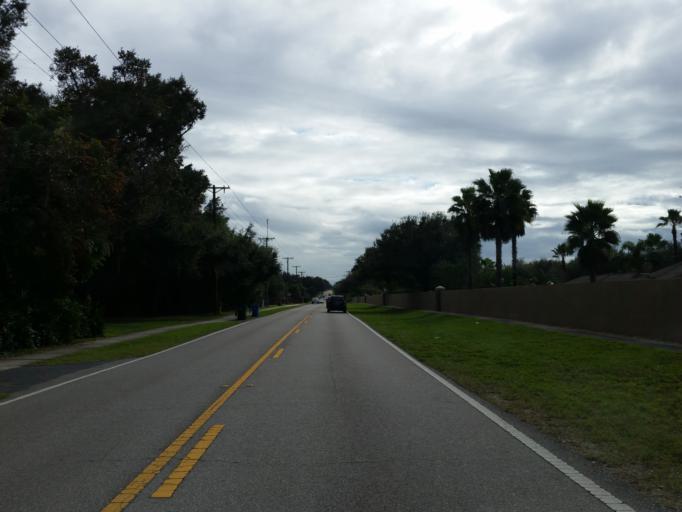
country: US
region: Florida
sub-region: Hillsborough County
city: Brandon
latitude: 27.9182
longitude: -82.2857
